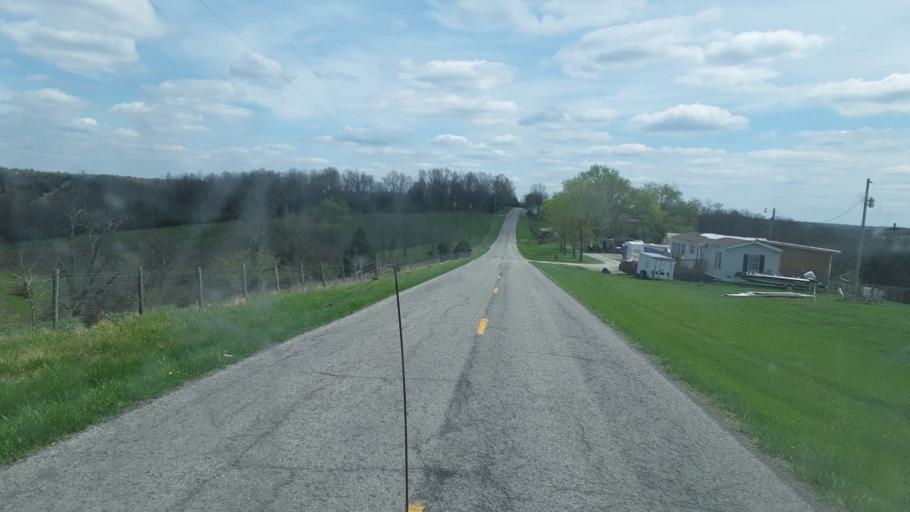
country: US
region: Kentucky
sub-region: Grant County
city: Dry Ridge
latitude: 38.6464
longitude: -84.7330
